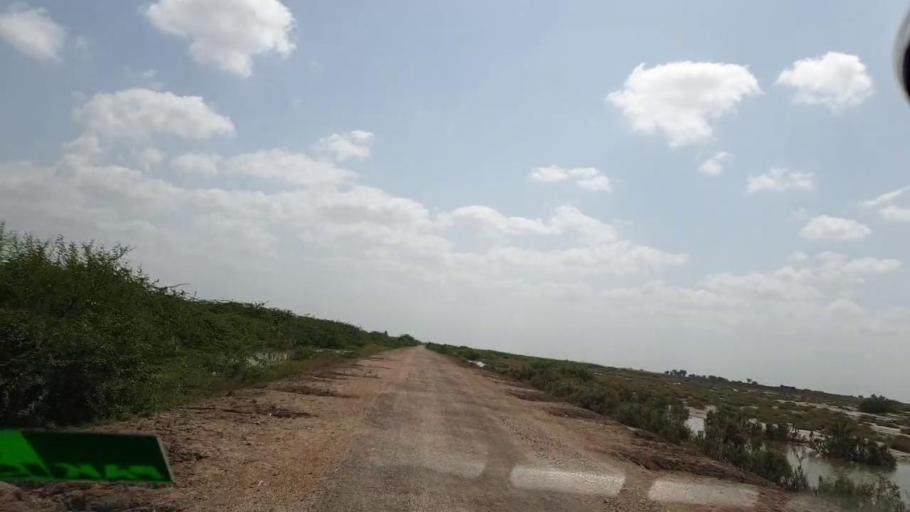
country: PK
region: Sindh
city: Kadhan
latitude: 24.5976
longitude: 69.1832
